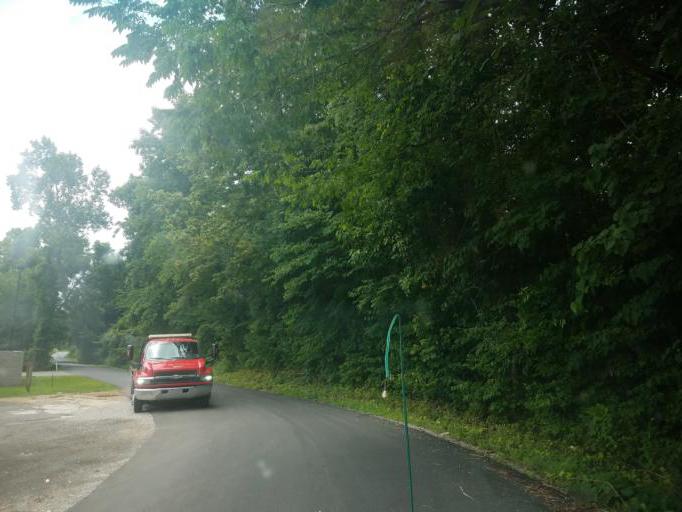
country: US
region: Kentucky
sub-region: Hart County
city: Munfordville
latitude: 37.2894
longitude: -85.9038
